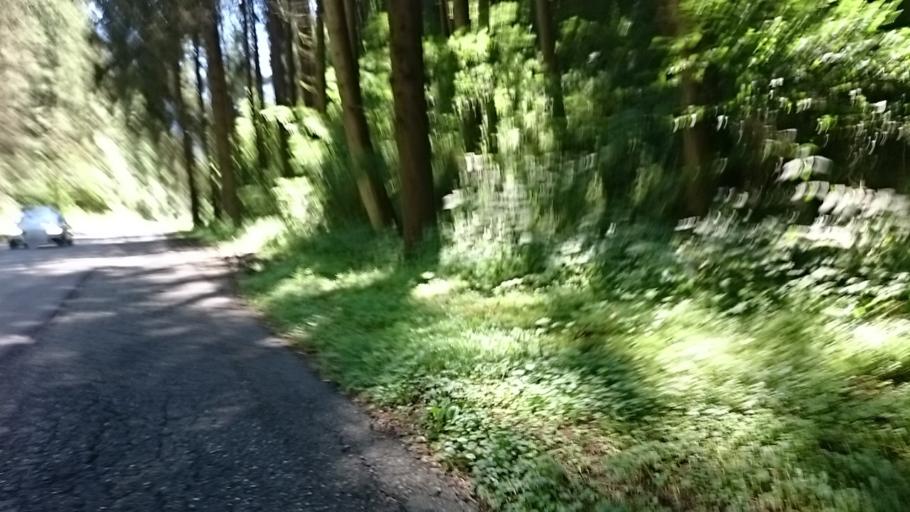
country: IT
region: Trentino-Alto Adige
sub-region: Bolzano
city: Falzes
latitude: 46.7826
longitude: 11.8759
